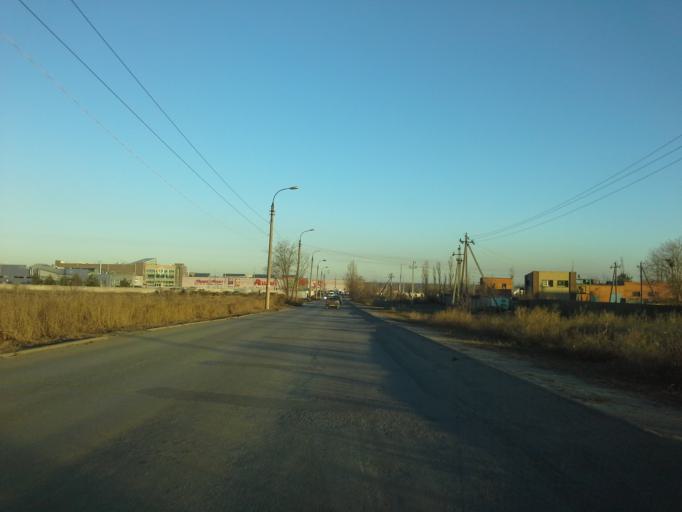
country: RU
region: Volgograd
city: Volgograd
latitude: 48.6370
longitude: 44.4258
